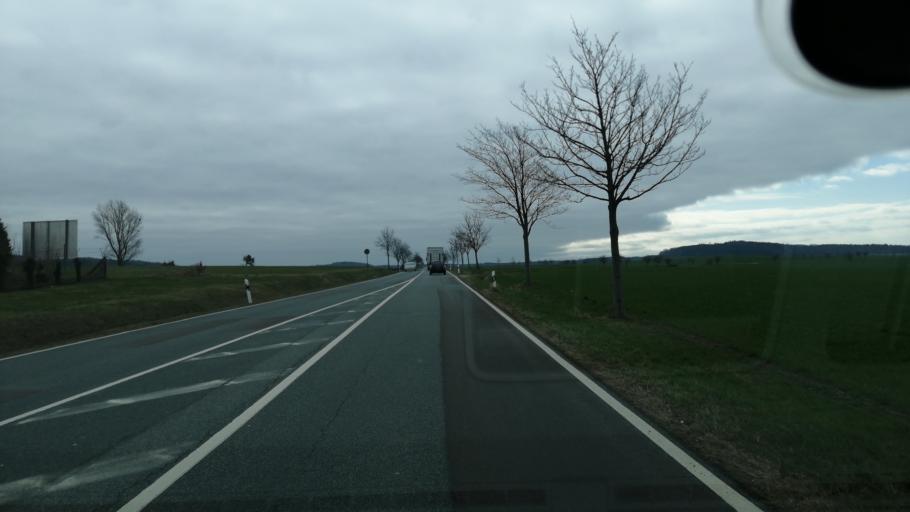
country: DE
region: Saxony
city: Lobau
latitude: 51.0751
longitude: 14.6795
